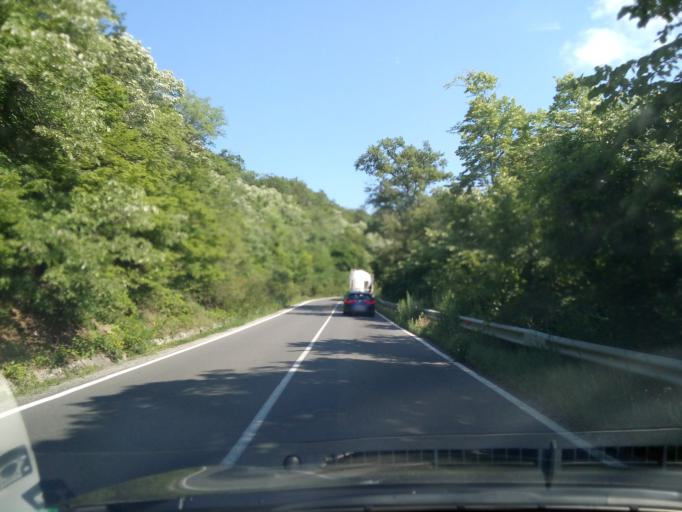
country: BG
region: Burgas
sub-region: Obshtina Nesebur
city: Sveti Vlas
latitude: 42.7369
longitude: 27.7389
